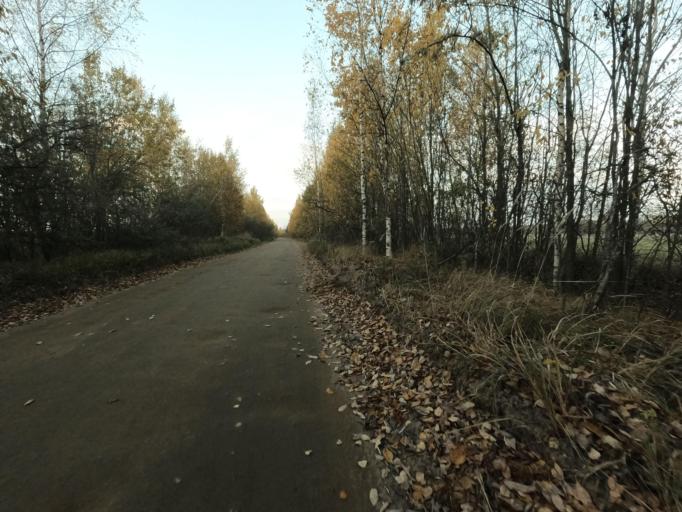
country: RU
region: Leningrad
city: Mga
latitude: 59.7942
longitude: 31.2007
